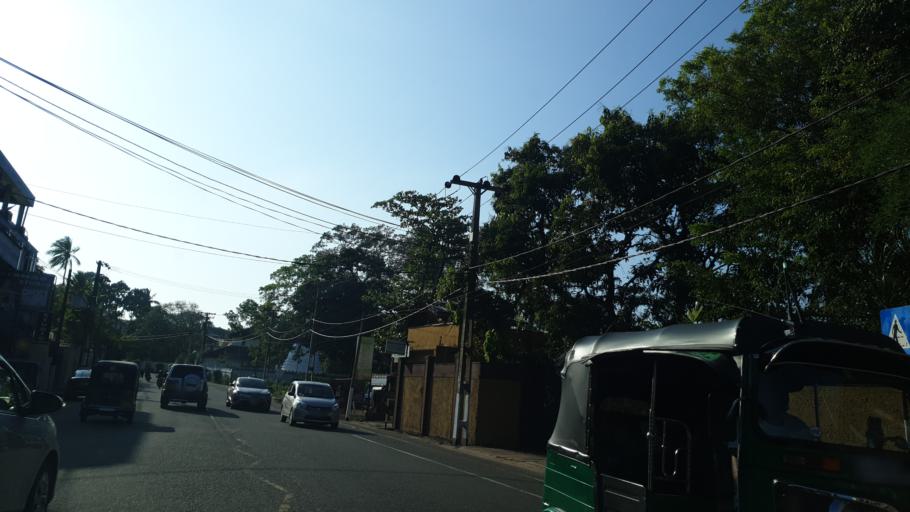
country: LK
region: Western
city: Sri Jayewardenepura Kotte
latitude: 6.8566
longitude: 79.8902
